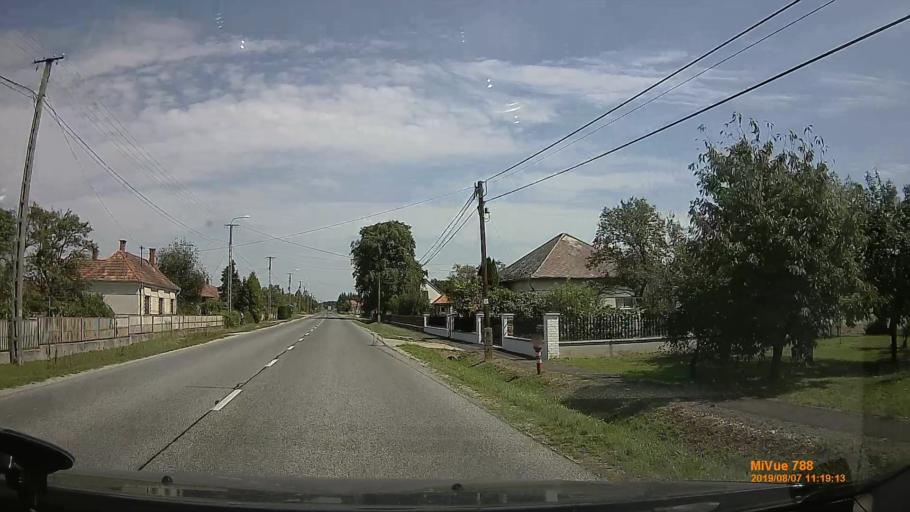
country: HU
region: Zala
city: Zalalovo
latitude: 46.7609
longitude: 16.5635
